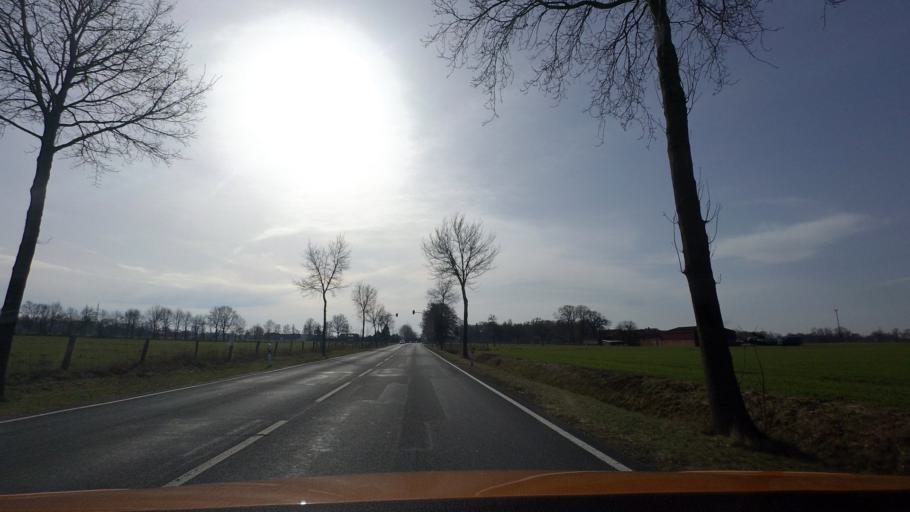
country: DE
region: Lower Saxony
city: Raddestorf
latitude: 52.4171
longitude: 8.9493
